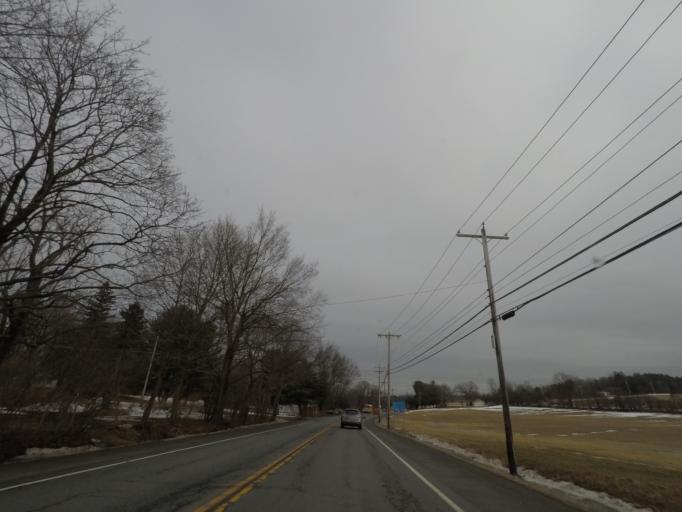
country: US
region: New York
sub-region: Albany County
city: Voorheesville
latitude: 42.7032
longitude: -73.9519
